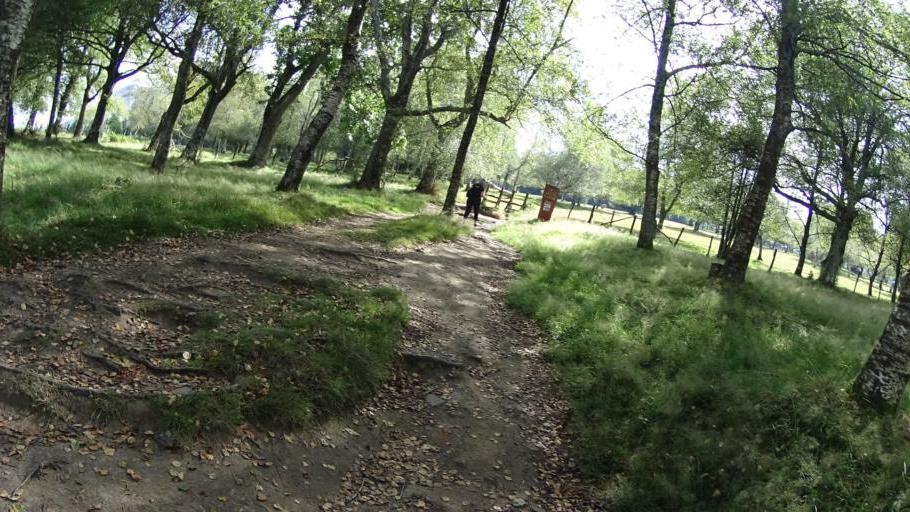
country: ES
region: Basque Country
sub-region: Bizkaia
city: Manaria
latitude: 43.0995
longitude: -2.6421
